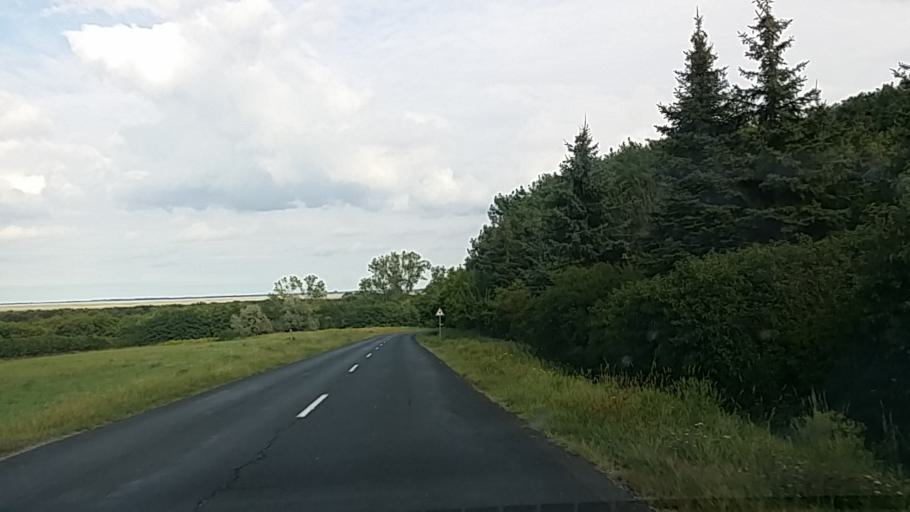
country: HU
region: Gyor-Moson-Sopron
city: Nagycenk
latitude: 47.6411
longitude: 16.6714
